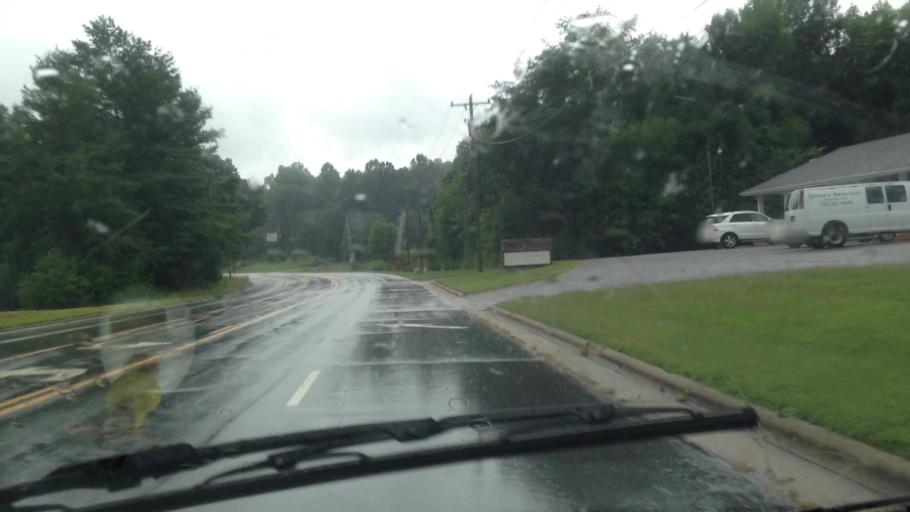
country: US
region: North Carolina
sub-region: Rockingham County
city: Mayodan
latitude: 36.4038
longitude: -79.9782
